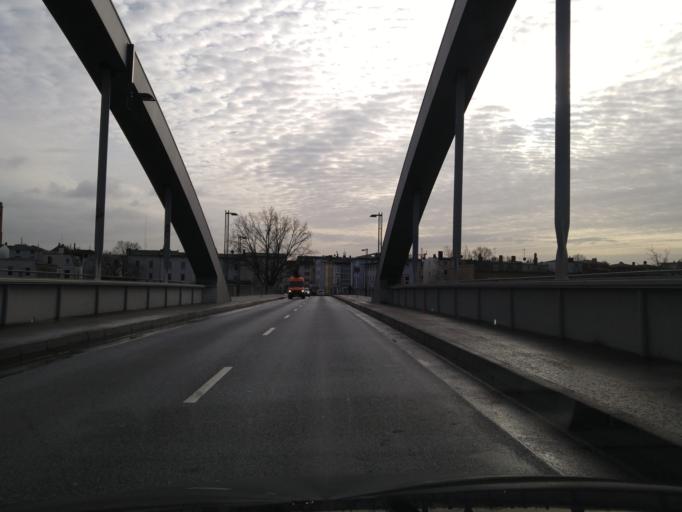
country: DE
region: Schleswig-Holstein
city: Luebeck
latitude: 53.8657
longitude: 10.6654
